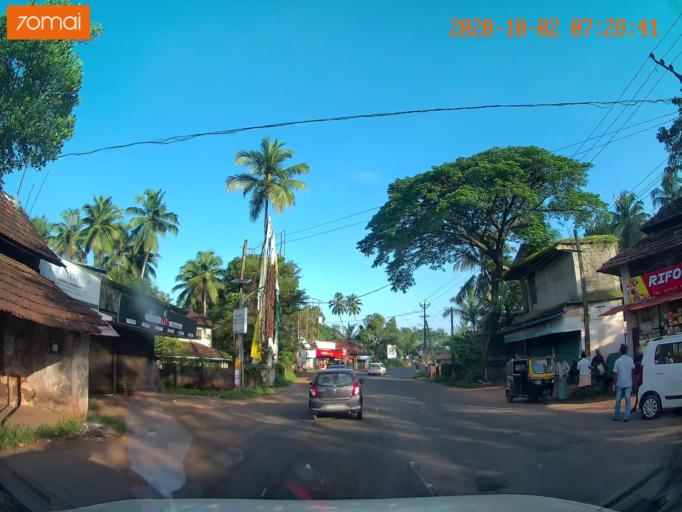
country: IN
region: Kerala
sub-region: Malappuram
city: Pariyapuram
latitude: 11.0297
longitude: 75.9417
